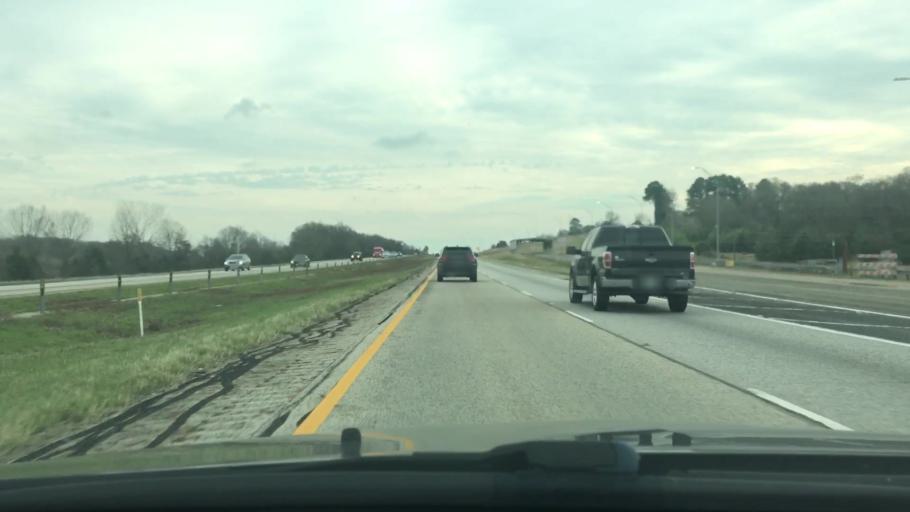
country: US
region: Texas
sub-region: Leon County
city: Centerville
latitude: 31.2814
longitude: -95.9916
